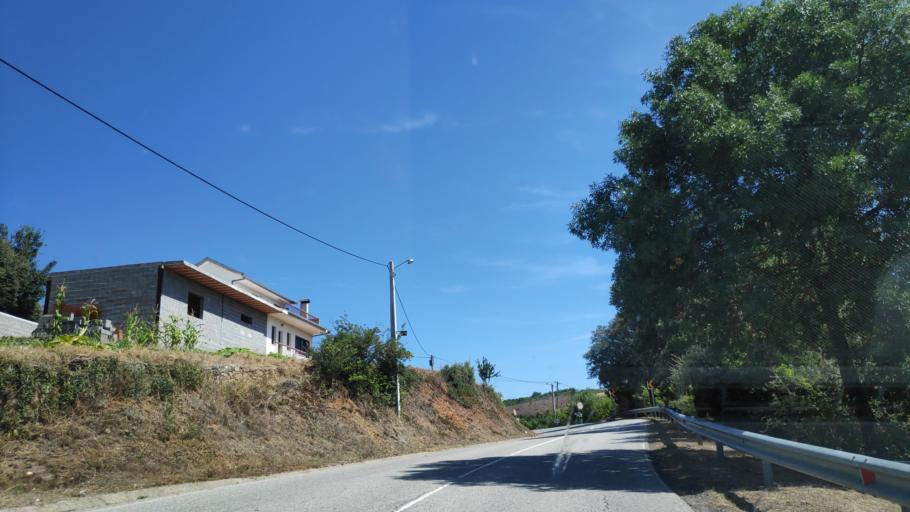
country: PT
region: Braganca
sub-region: Braganca Municipality
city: Braganca
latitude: 41.8381
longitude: -6.7468
